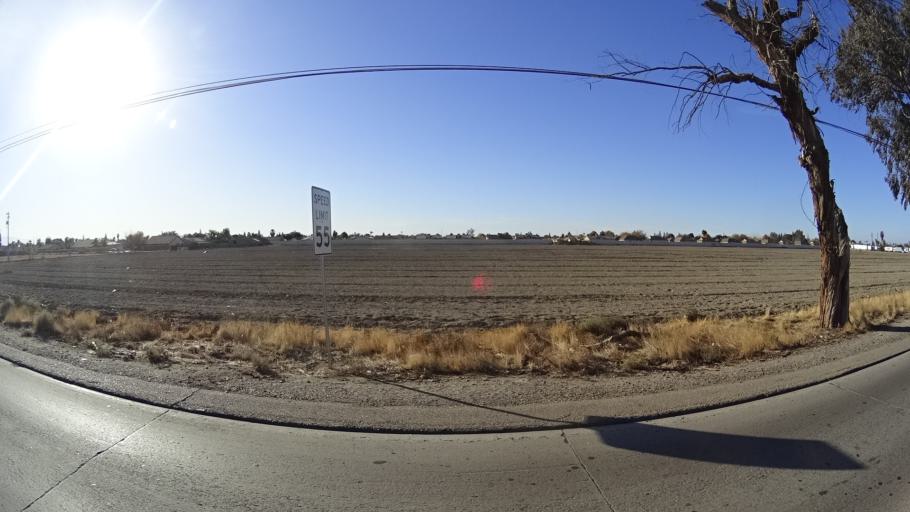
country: US
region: California
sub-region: Kern County
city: Greenfield
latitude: 35.3004
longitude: -119.0031
